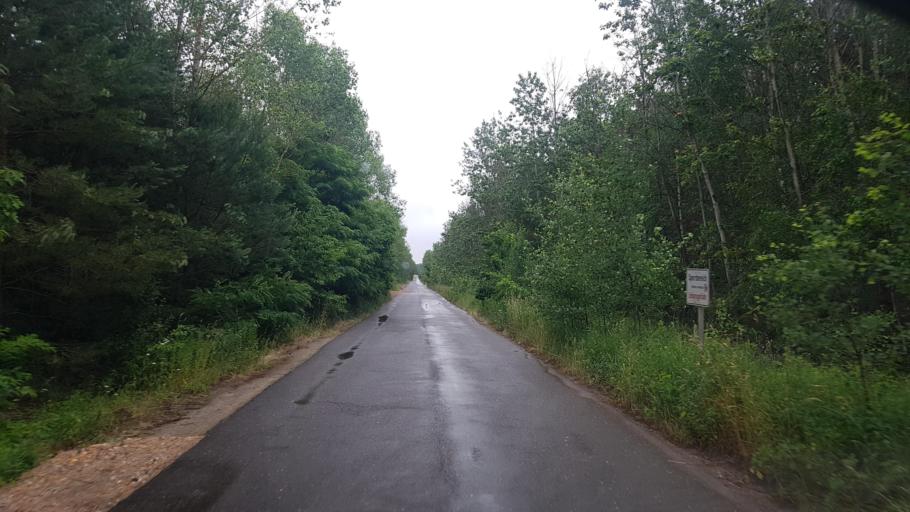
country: DE
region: Brandenburg
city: Lauchhammer
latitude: 51.5404
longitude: 13.7541
